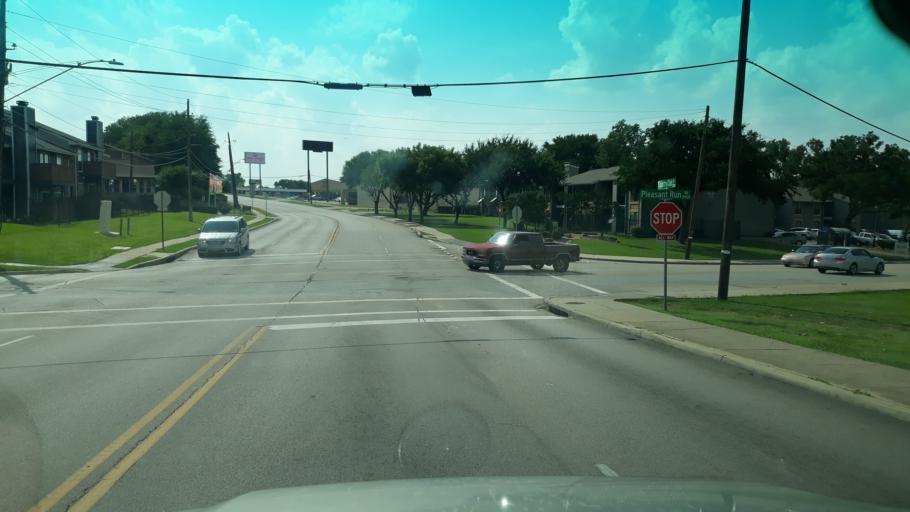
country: US
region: Texas
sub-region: Dallas County
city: Irving
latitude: 32.8602
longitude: -96.9883
